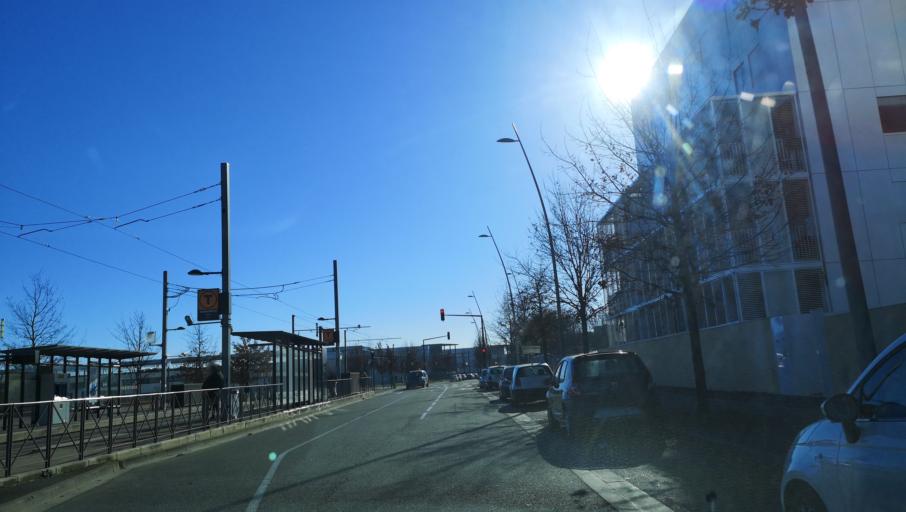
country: FR
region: Midi-Pyrenees
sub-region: Departement de la Haute-Garonne
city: Beauzelle
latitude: 43.6549
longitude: 1.3732
